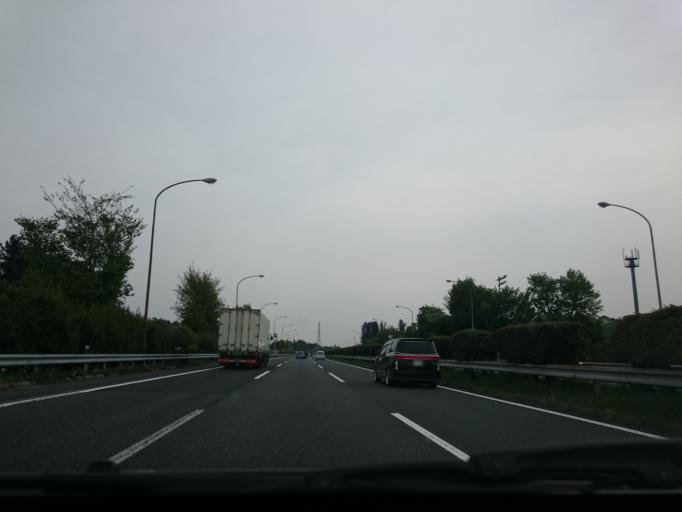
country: JP
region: Tochigi
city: Utsunomiya-shi
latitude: 36.6002
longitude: 139.8435
